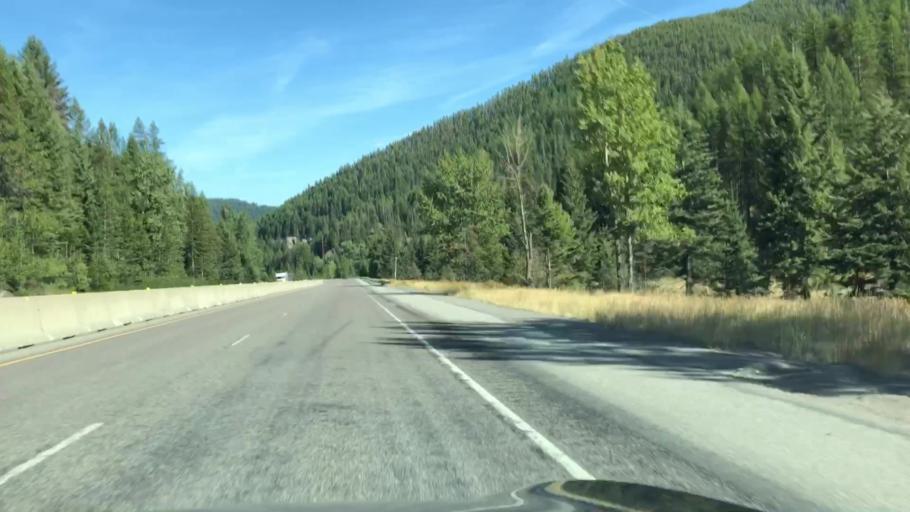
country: US
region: Montana
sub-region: Sanders County
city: Thompson Falls
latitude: 47.4174
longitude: -115.5525
